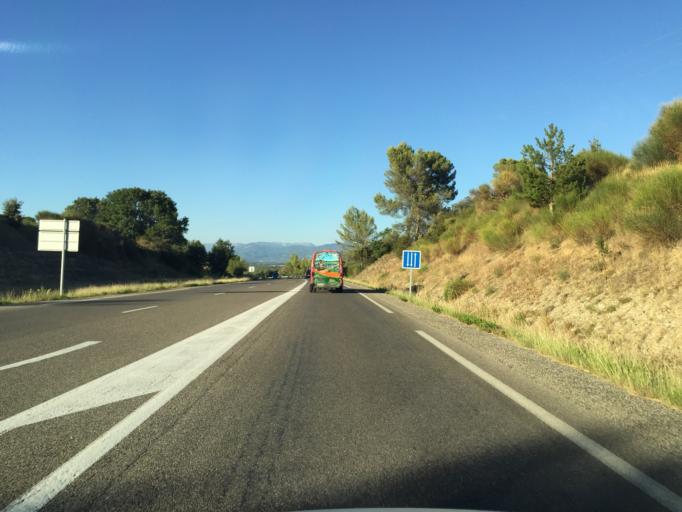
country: FR
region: Provence-Alpes-Cote d'Azur
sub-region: Departement des Alpes-de-Haute-Provence
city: Oraison
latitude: 43.9606
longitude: 5.8993
